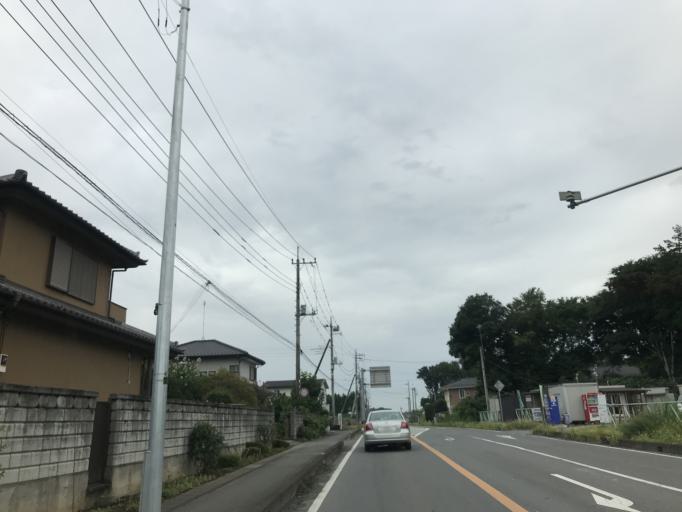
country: JP
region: Ibaraki
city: Sakai
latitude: 36.1240
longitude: 139.7926
